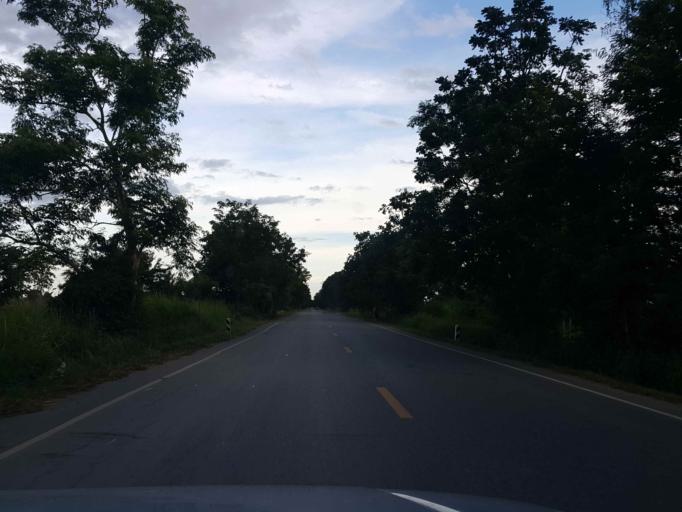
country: TH
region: Sukhothai
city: Sawankhalok
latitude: 17.3795
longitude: 99.7377
